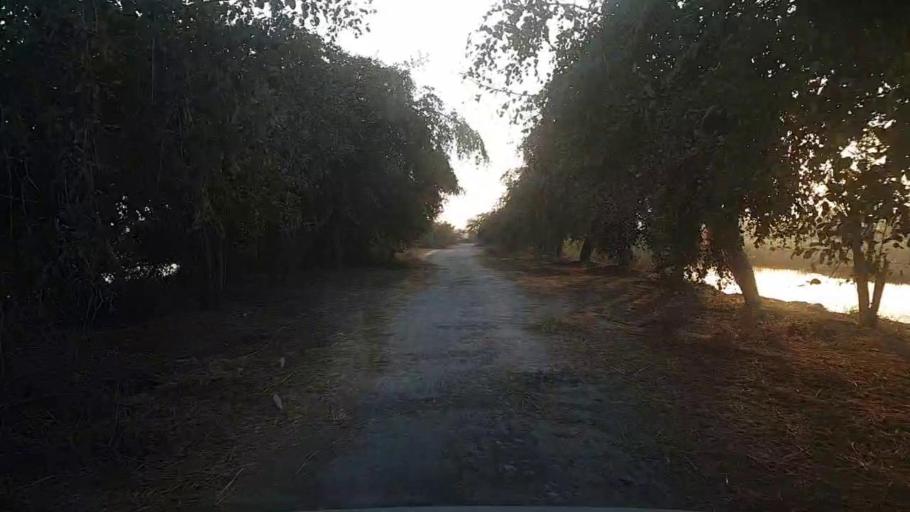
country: PK
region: Sindh
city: Mehar
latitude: 27.1857
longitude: 67.7398
